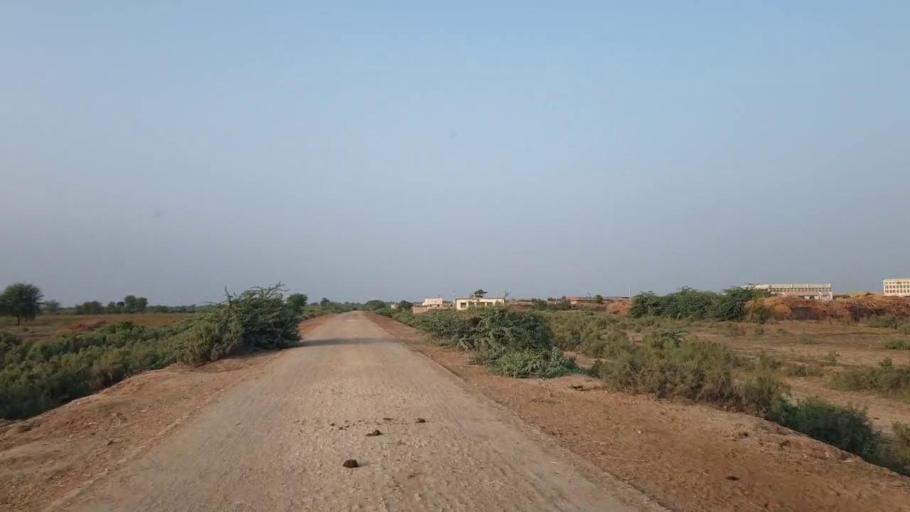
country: PK
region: Sindh
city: Tando Ghulam Ali
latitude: 25.0498
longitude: 68.9645
